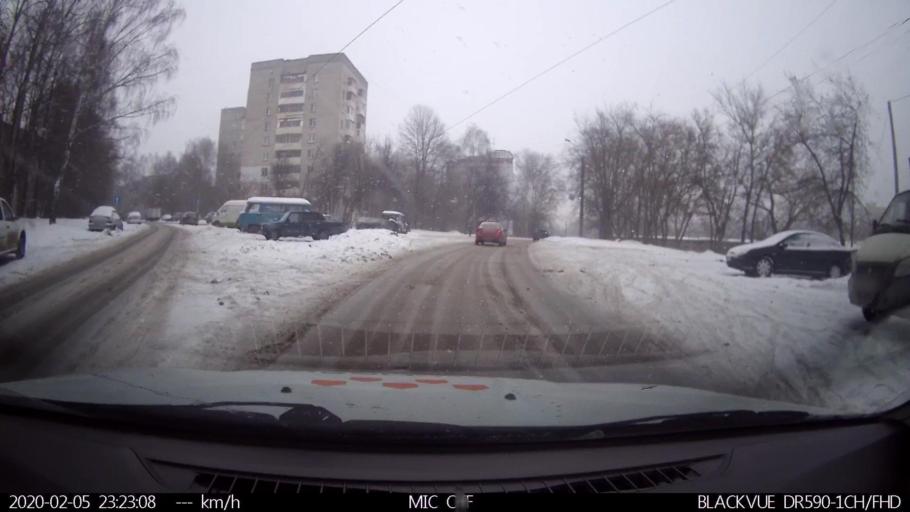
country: RU
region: Nizjnij Novgorod
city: Nizhniy Novgorod
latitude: 56.2893
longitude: 44.0417
